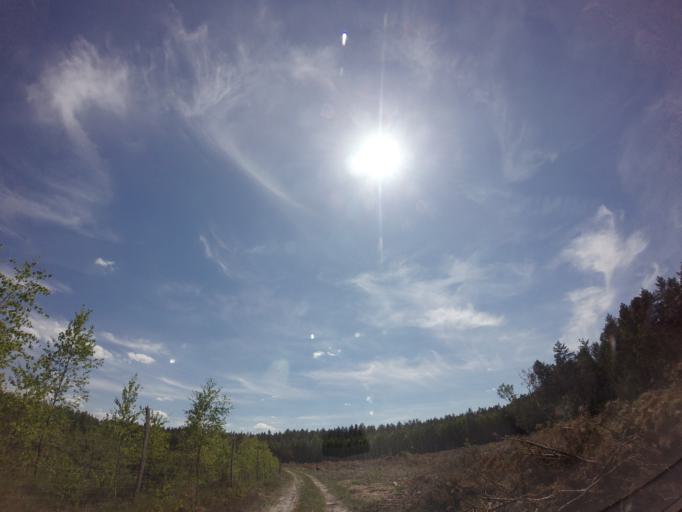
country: PL
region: West Pomeranian Voivodeship
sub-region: Powiat drawski
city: Kalisz Pomorski
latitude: 53.1661
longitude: 15.9037
